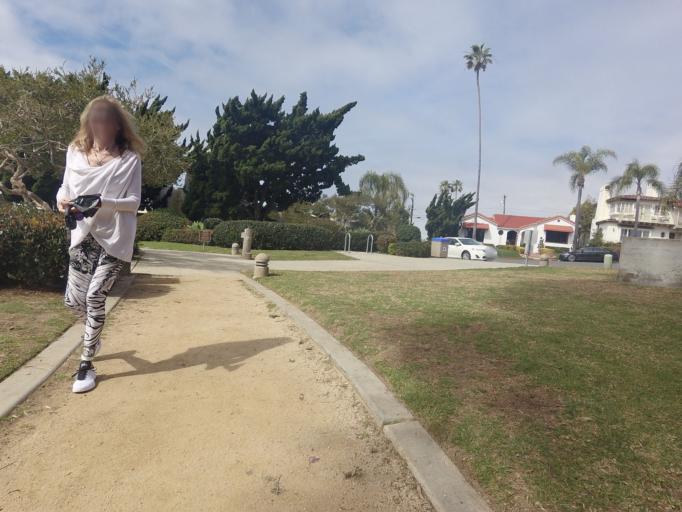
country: US
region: California
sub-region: Orange County
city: Laguna Beach
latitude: 33.5471
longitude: -117.8038
